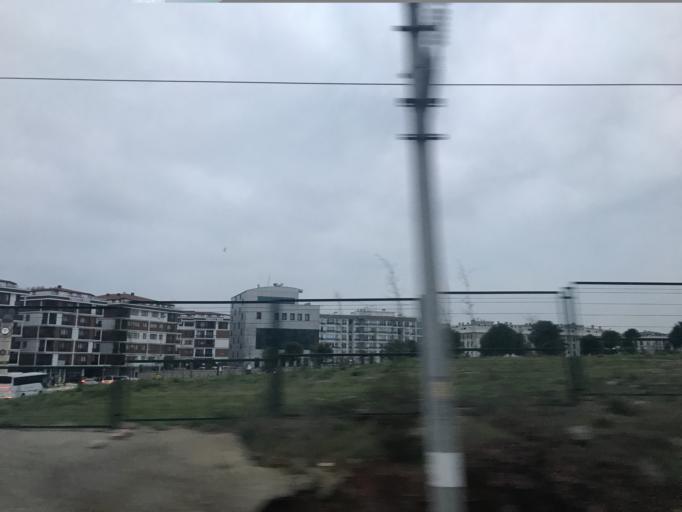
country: TR
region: Istanbul
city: Icmeler
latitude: 40.8430
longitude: 29.3032
